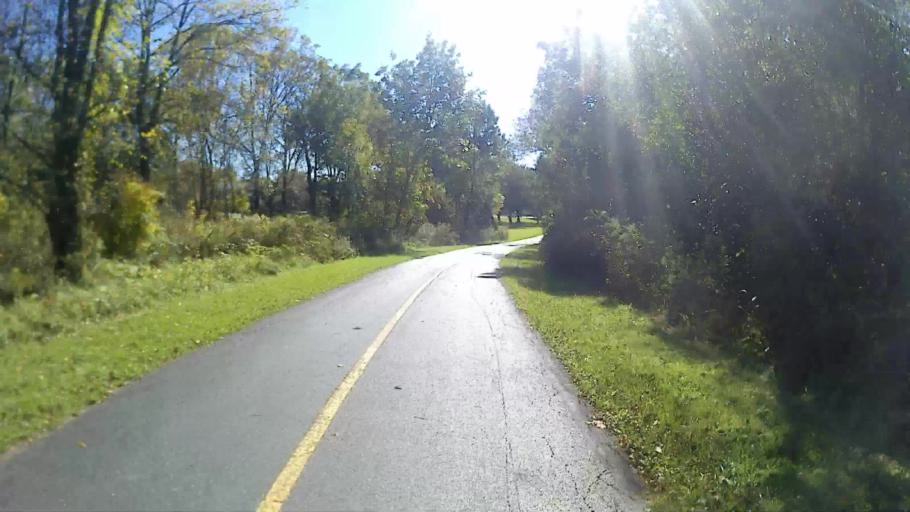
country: US
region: Illinois
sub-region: Cook County
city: Elk Grove Village
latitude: 42.0182
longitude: -87.9923
